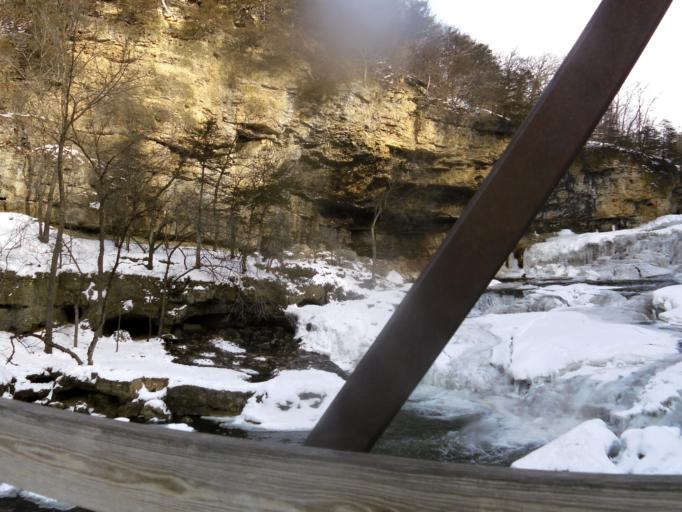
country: US
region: Wisconsin
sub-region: Saint Croix County
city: North Hudson
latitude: 45.0244
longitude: -92.6654
